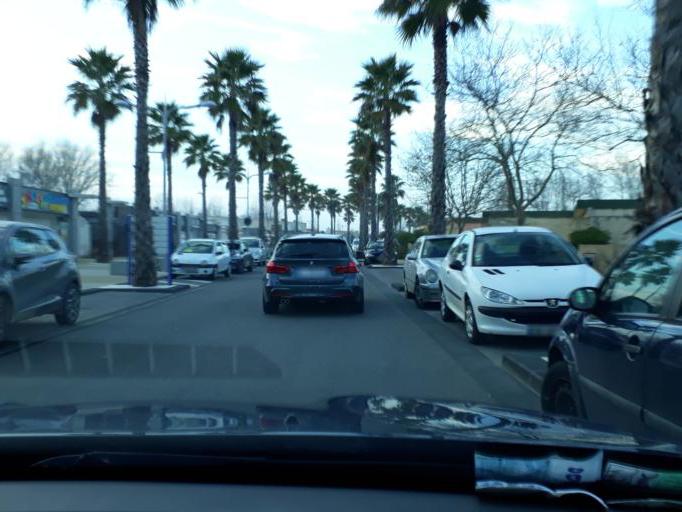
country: FR
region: Languedoc-Roussillon
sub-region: Departement de l'Herault
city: Marseillan
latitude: 43.3167
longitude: 3.5492
